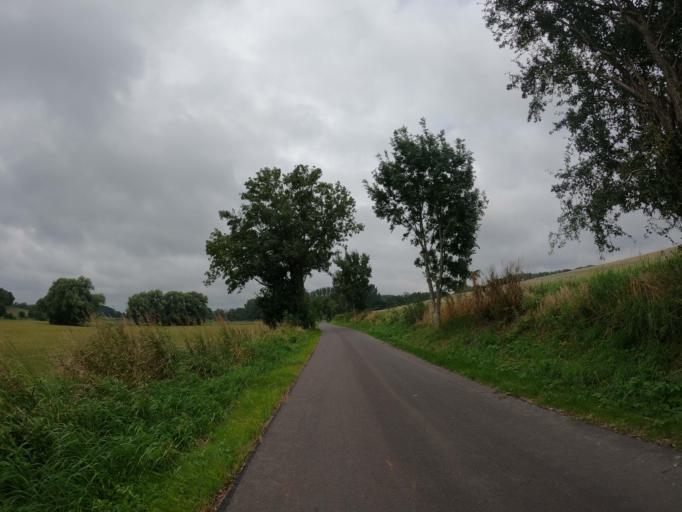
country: DE
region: Mecklenburg-Vorpommern
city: Poseritz
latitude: 54.2945
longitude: 13.2151
